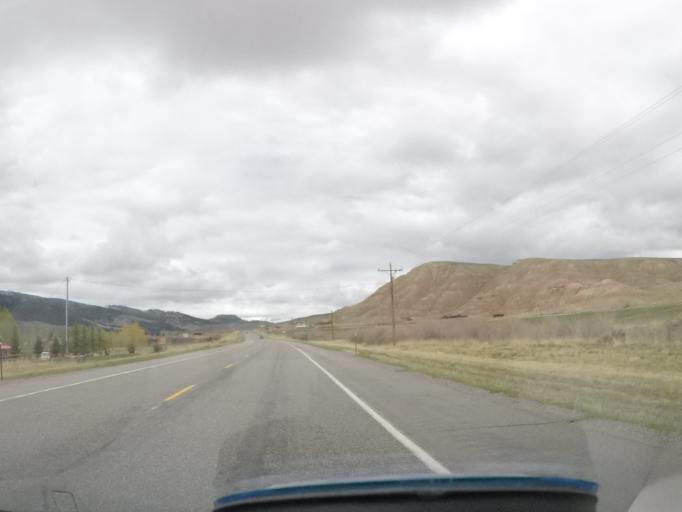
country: US
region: Wyoming
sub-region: Sublette County
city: Pinedale
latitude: 43.5675
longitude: -109.7091
